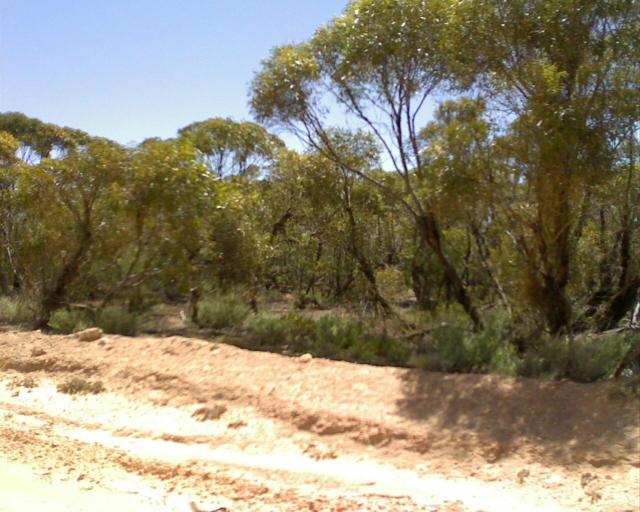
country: AU
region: South Australia
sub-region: Kimba
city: Caralue
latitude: -32.9447
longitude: 135.2709
